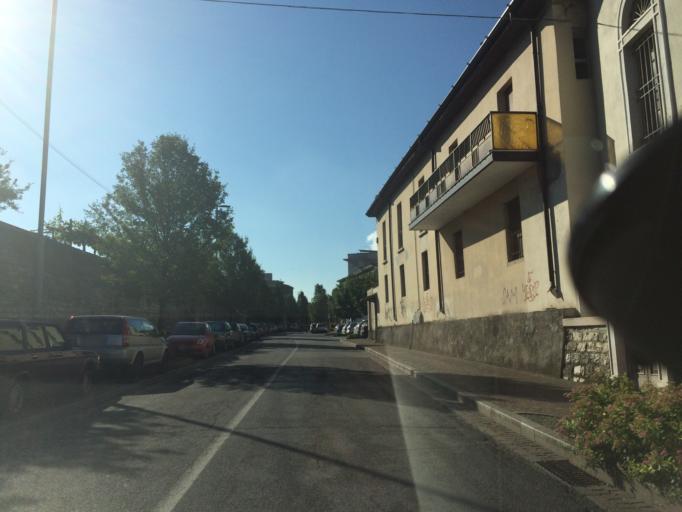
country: IT
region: Lombardy
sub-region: Provincia di Brescia
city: Brescia
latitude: 45.5326
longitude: 10.2092
